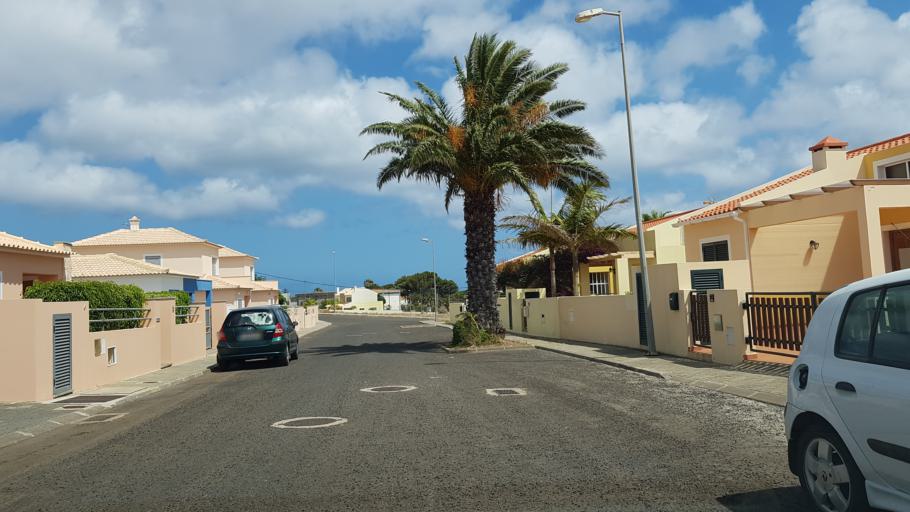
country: PT
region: Madeira
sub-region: Porto Santo
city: Vila de Porto Santo
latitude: 33.0621
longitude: -16.3420
